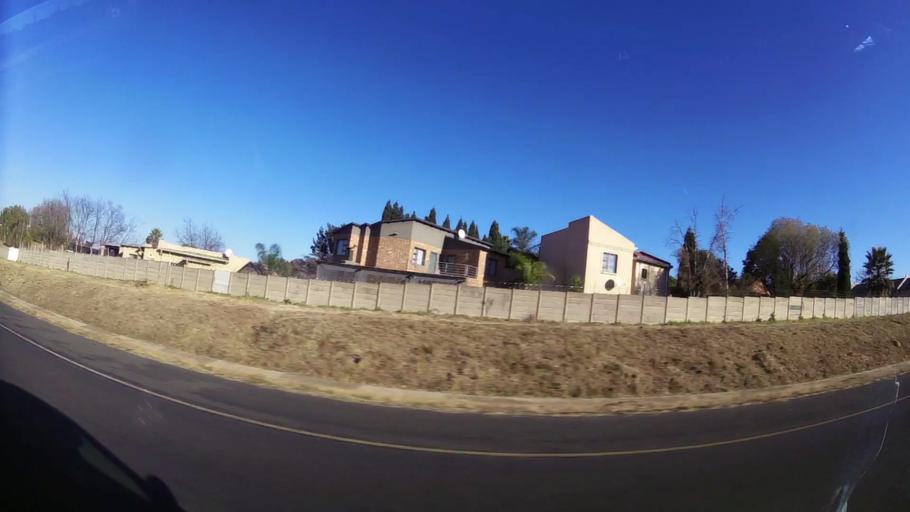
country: ZA
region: Gauteng
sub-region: City of Johannesburg Metropolitan Municipality
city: Modderfontein
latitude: -26.0847
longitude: 28.2047
